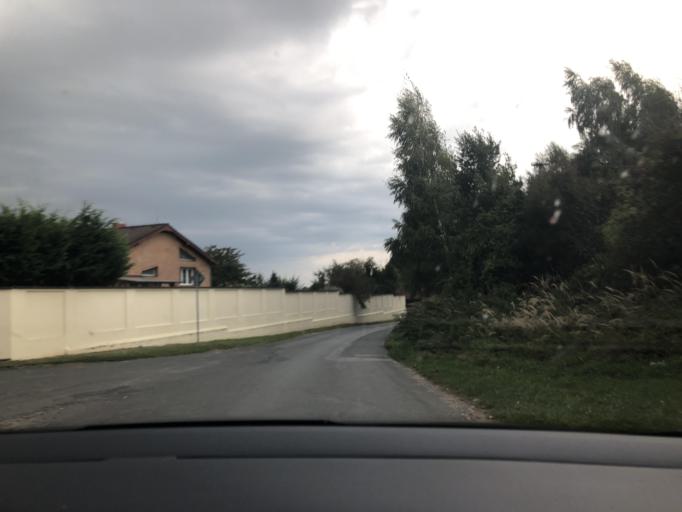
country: CZ
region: Central Bohemia
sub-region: Okres Kolin
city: Tynec nad Labem
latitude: 50.0346
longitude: 15.3618
